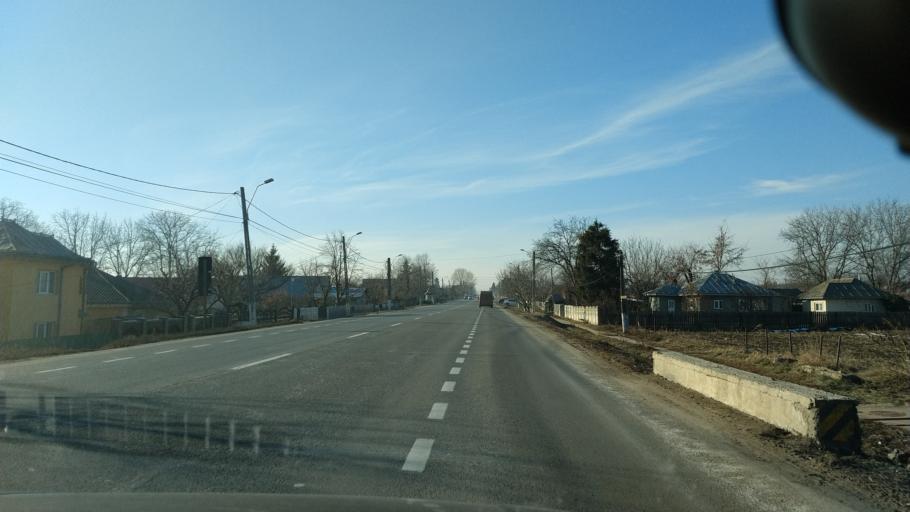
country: RO
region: Iasi
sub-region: Comuna Ion Neculce
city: Razboieni
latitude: 47.2190
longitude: 27.0572
